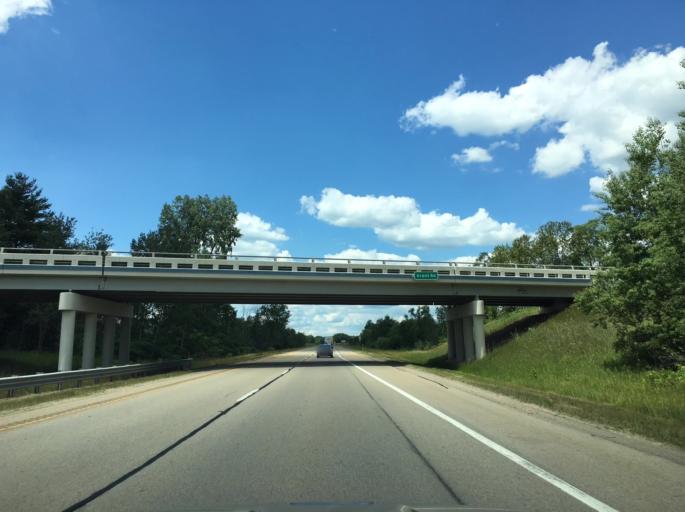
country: US
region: Michigan
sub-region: Clare County
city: Clare
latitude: 43.8814
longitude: -84.7875
